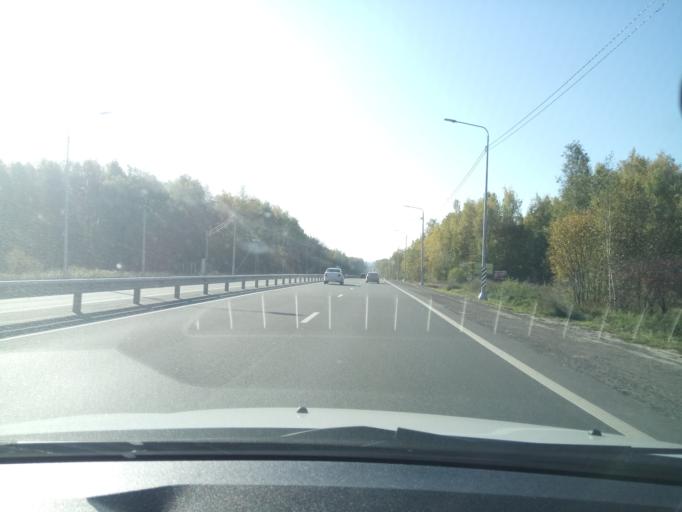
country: RU
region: Nizjnij Novgorod
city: Burevestnik
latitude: 56.0326
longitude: 43.9618
